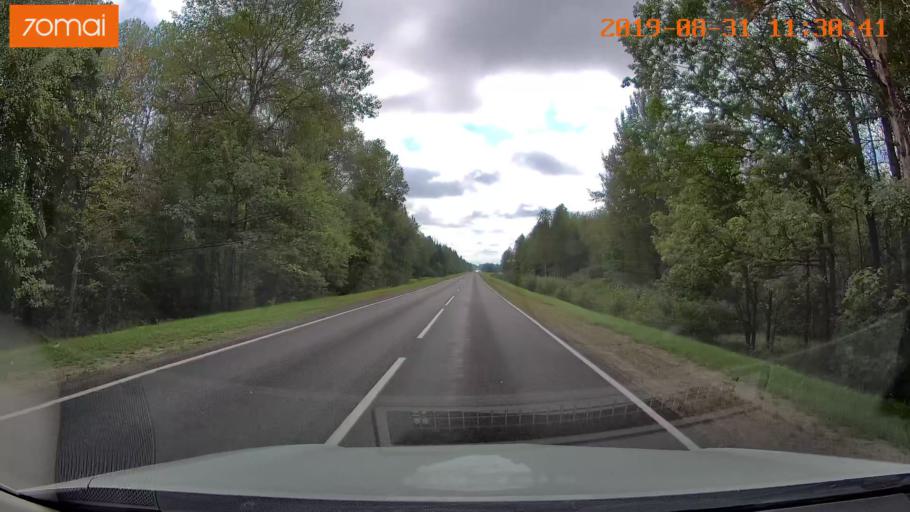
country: BY
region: Mogilev
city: Chavusy
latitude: 53.7146
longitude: 31.1366
